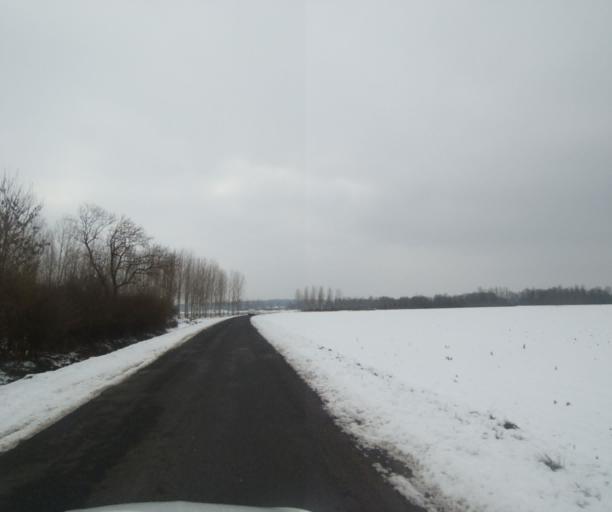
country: FR
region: Champagne-Ardenne
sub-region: Departement de la Haute-Marne
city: Saint-Dizier
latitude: 48.5737
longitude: 4.8901
